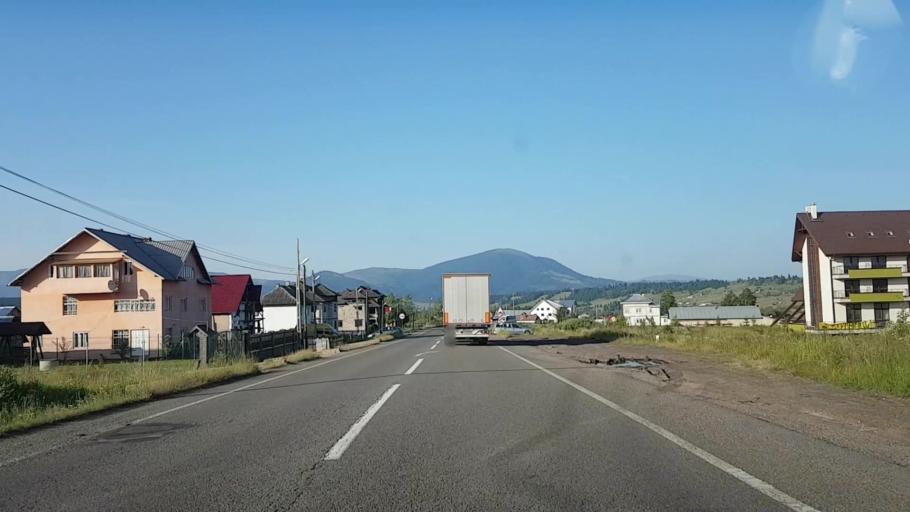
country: RO
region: Suceava
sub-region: Comuna Poiana Stampei
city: Poiana Stampei
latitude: 47.3275
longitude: 25.1448
